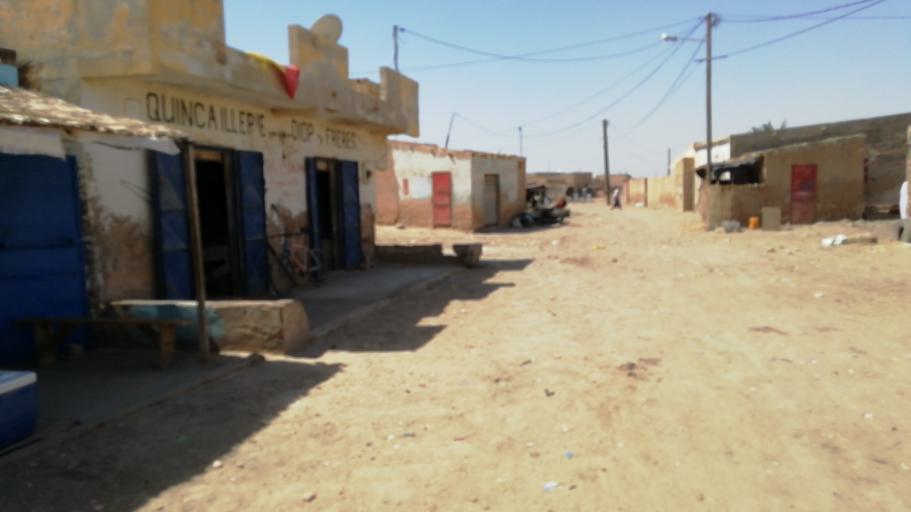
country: SN
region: Saint-Louis
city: Rosso
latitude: 16.4005
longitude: -16.0760
